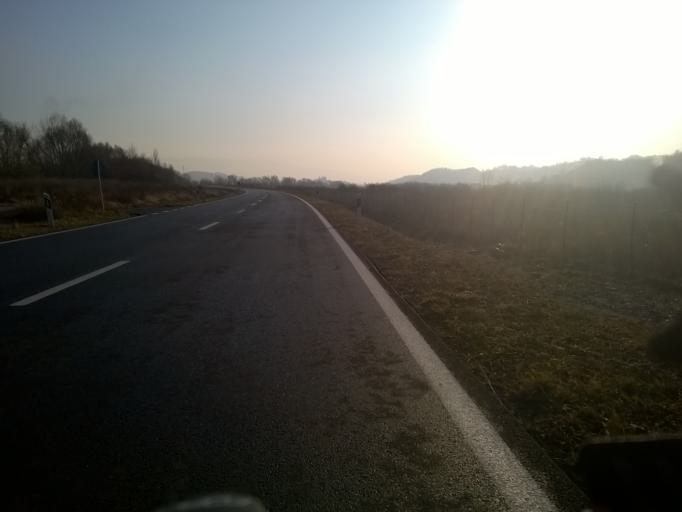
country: HR
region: Krapinsko-Zagorska
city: Zabok
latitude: 46.0661
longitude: 15.9135
